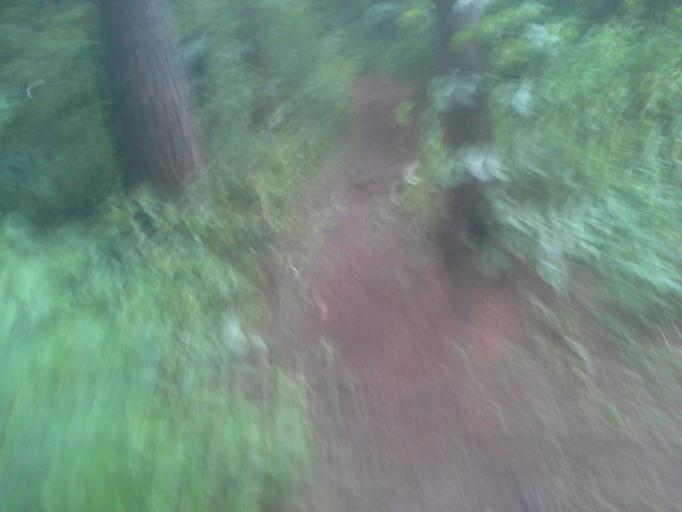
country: RU
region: Moskovskaya
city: Zhavoronki
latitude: 55.6639
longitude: 37.1024
